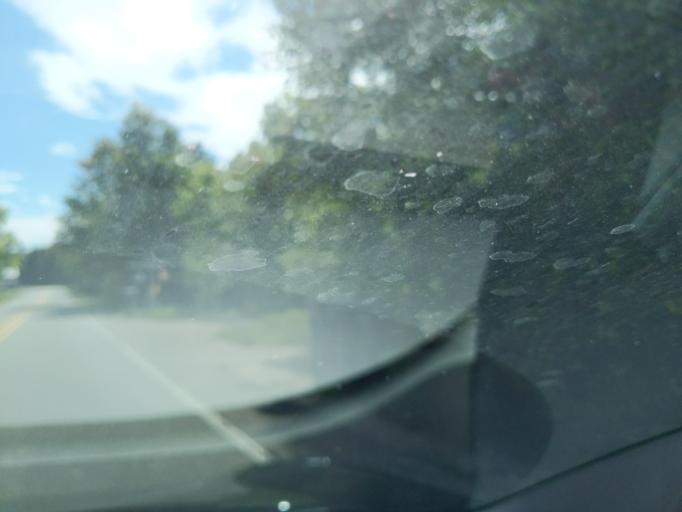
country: US
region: Michigan
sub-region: Antrim County
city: Bellaire
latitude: 45.0611
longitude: -85.3183
